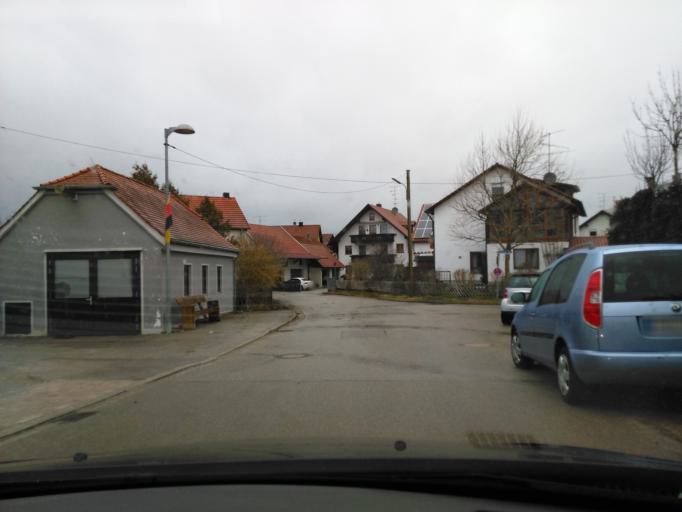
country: DE
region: Bavaria
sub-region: Upper Bavaria
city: Fuerstenfeldbruck
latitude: 48.1896
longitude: 11.2209
